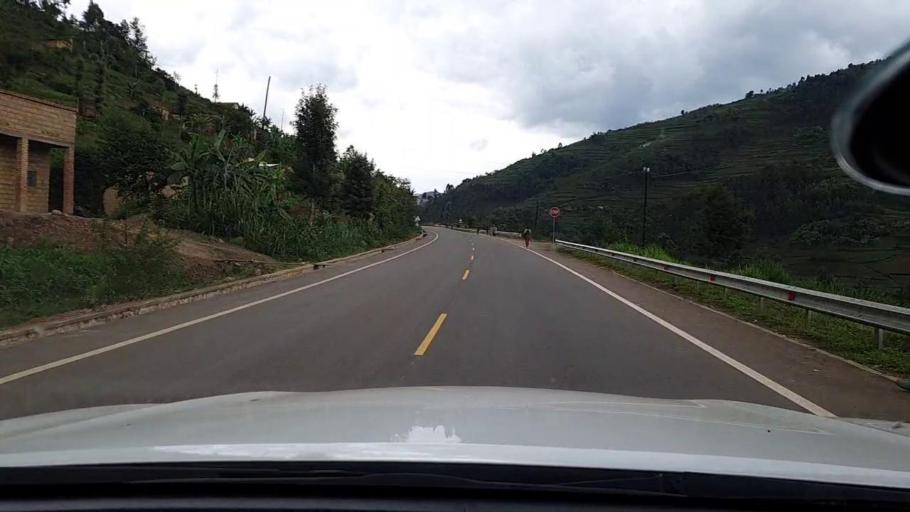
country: RW
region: Northern Province
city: Byumba
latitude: -1.6462
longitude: 29.9235
